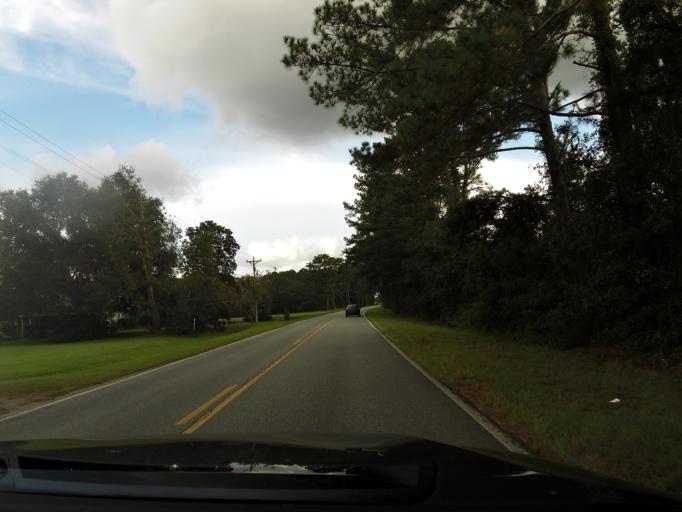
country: US
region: Georgia
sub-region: Liberty County
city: Midway
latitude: 31.8570
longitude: -81.4273
